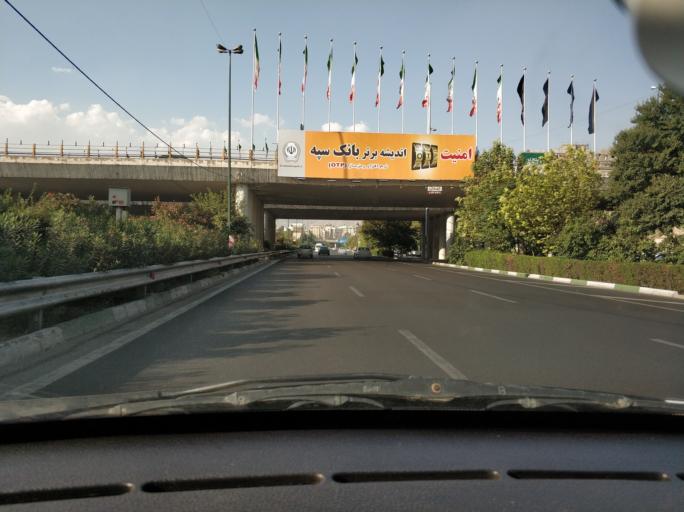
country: IR
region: Tehran
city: Tajrish
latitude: 35.7562
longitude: 51.4654
